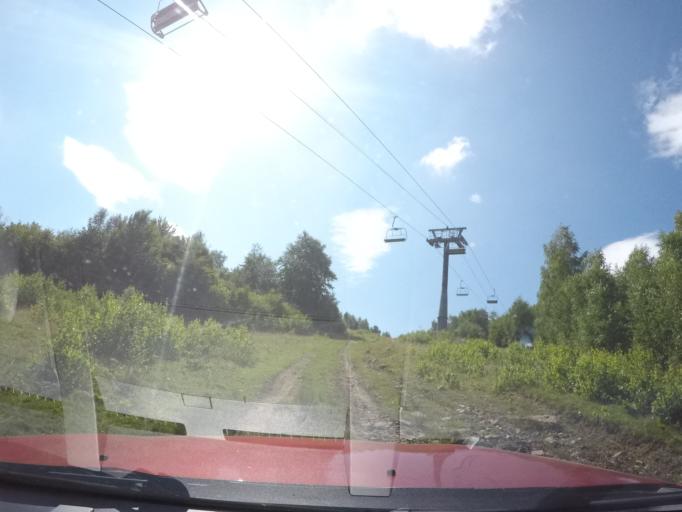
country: UA
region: Zakarpattia
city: Velykyi Bereznyi
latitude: 48.9384
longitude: 22.6665
